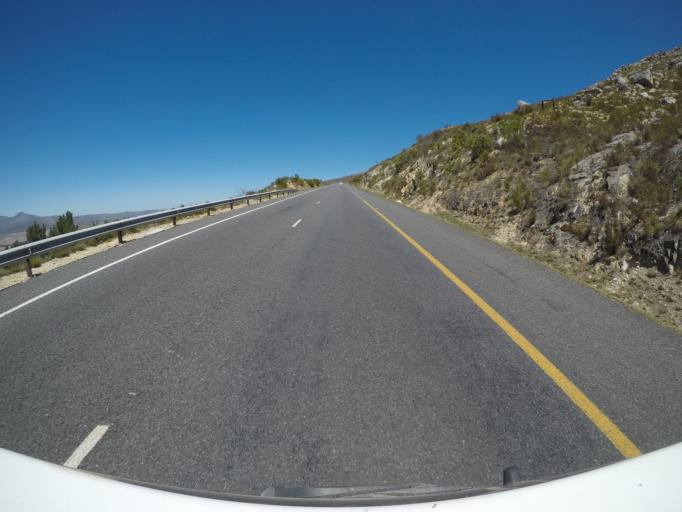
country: ZA
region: Western Cape
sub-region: Overberg District Municipality
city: Grabouw
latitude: -34.2193
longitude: 19.1854
